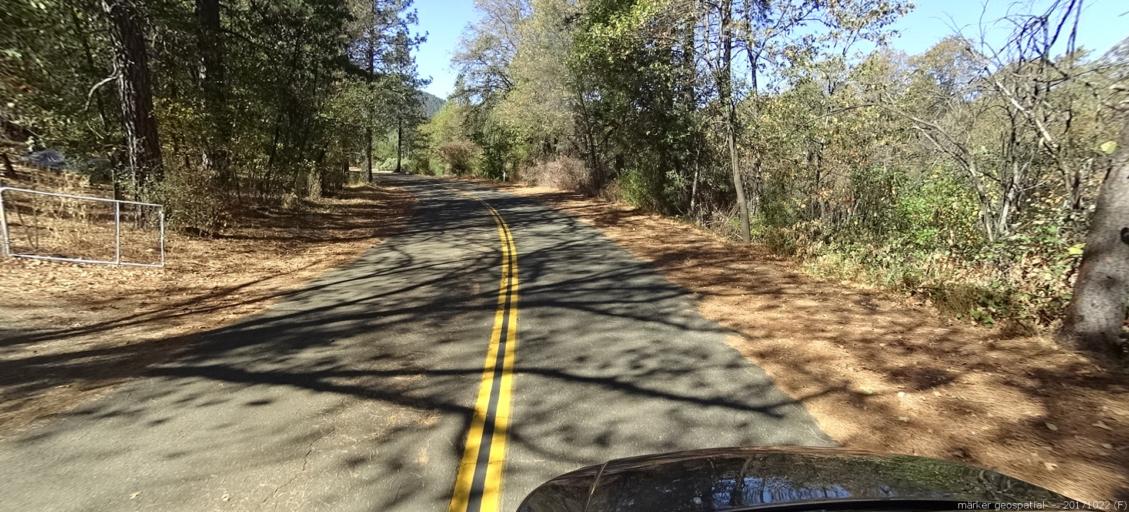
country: US
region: California
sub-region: Shasta County
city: Central Valley (historical)
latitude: 40.9168
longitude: -122.3878
